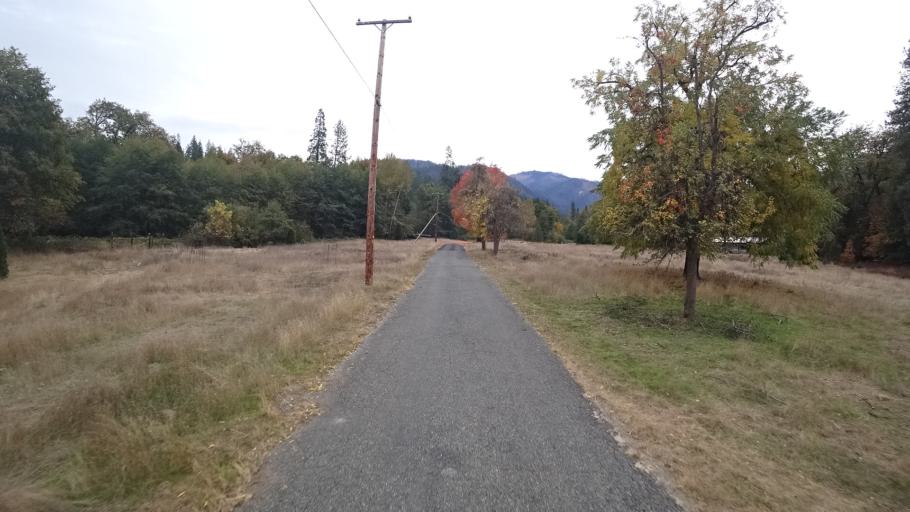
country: US
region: California
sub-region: Siskiyou County
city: Happy Camp
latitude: 41.8383
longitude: -123.2086
